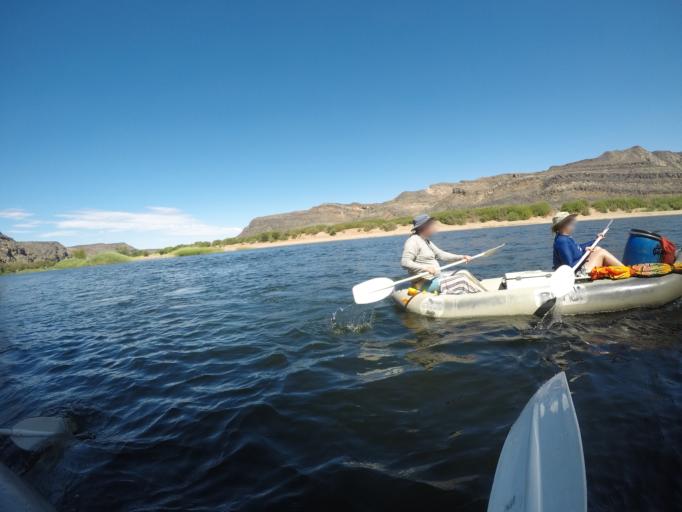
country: ZA
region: Northern Cape
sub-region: Namakwa District Municipality
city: Port Nolloth
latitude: -28.6995
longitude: 17.4789
